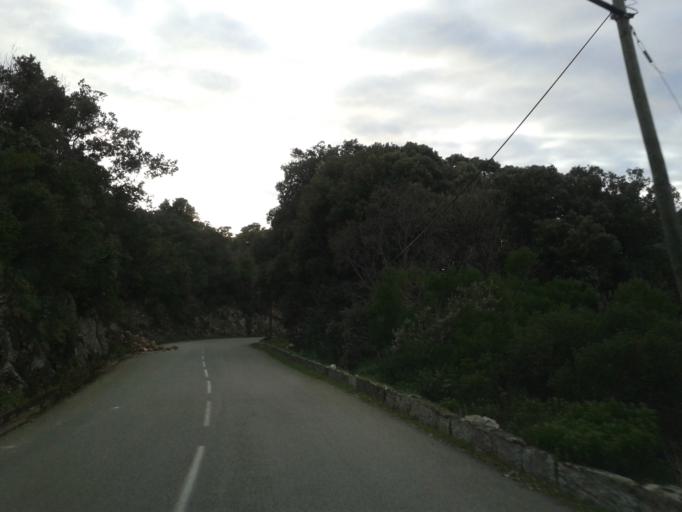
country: FR
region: Corsica
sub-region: Departement de la Haute-Corse
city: Brando
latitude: 42.8673
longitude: 9.3496
